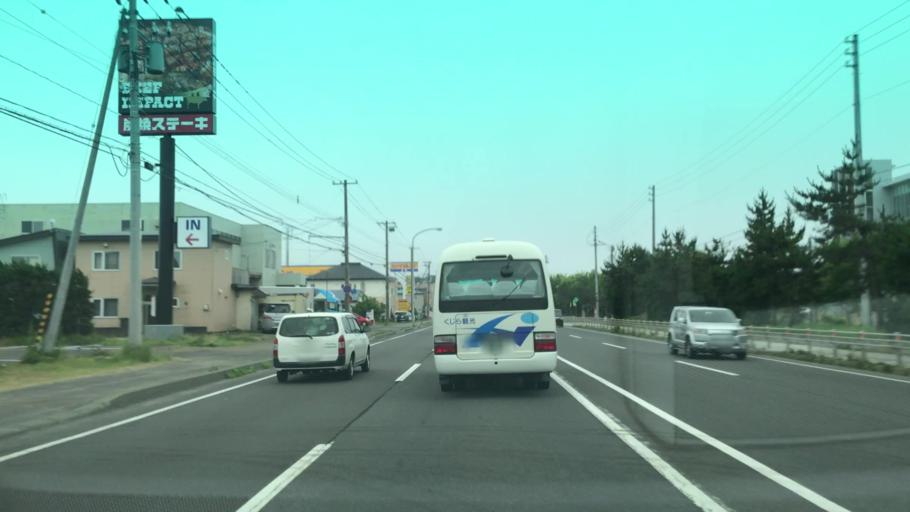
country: JP
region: Hokkaido
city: Muroran
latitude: 42.3612
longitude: 141.0545
